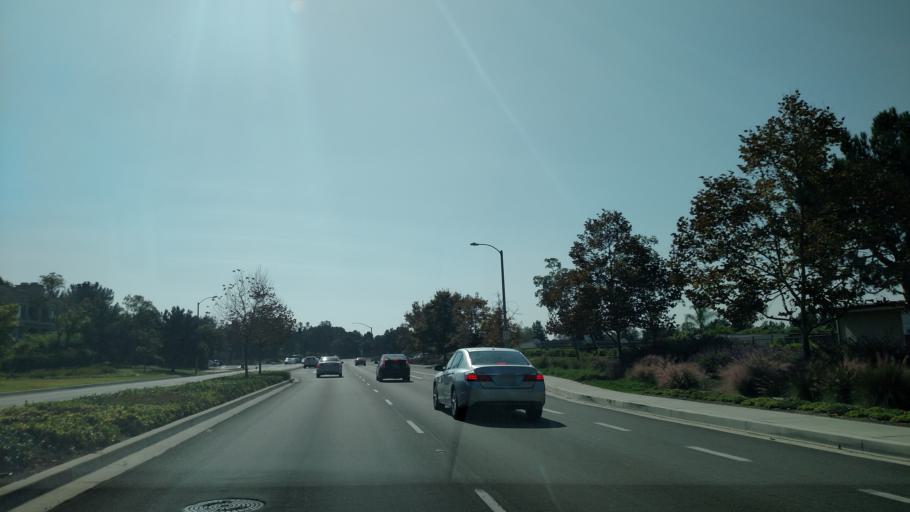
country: US
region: California
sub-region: Orange County
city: Irvine
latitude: 33.6896
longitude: -117.8174
